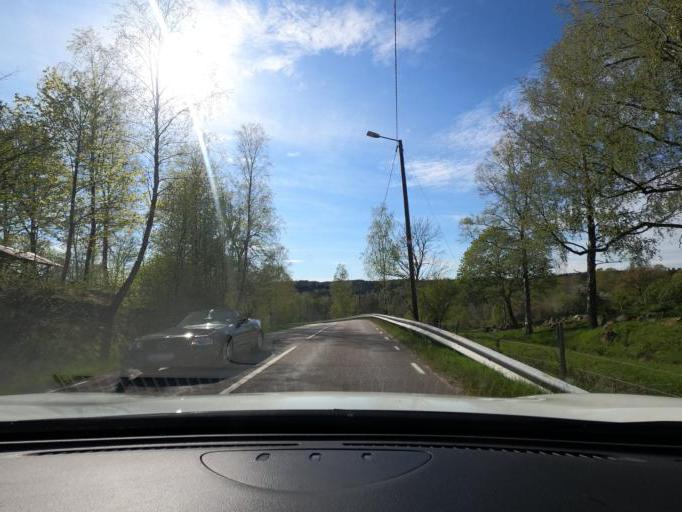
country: SE
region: Vaestra Goetaland
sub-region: Harryda Kommun
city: Landvetter
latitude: 57.6159
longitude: 12.2949
